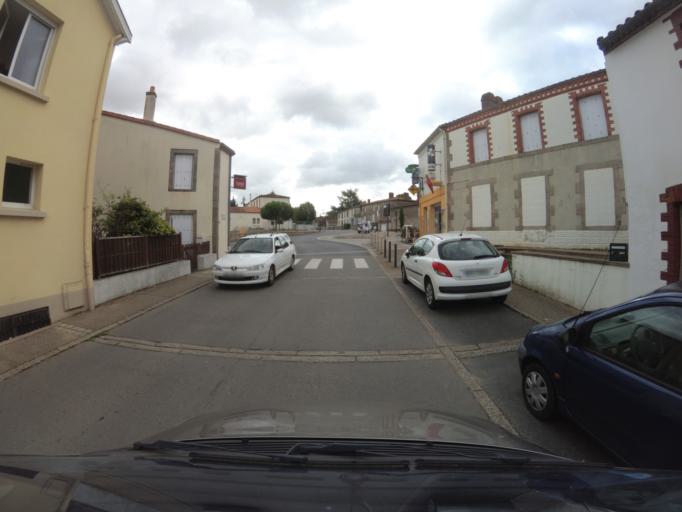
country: FR
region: Pays de la Loire
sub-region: Departement de la Loire-Atlantique
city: Getigne
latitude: 47.0755
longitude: -1.2486
